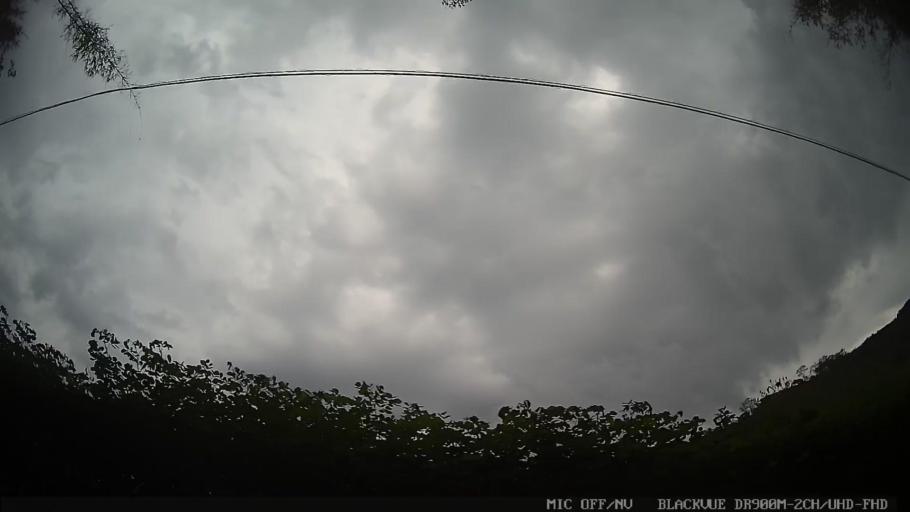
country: BR
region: Sao Paulo
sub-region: Itatiba
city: Itatiba
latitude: -23.0255
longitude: -46.8918
